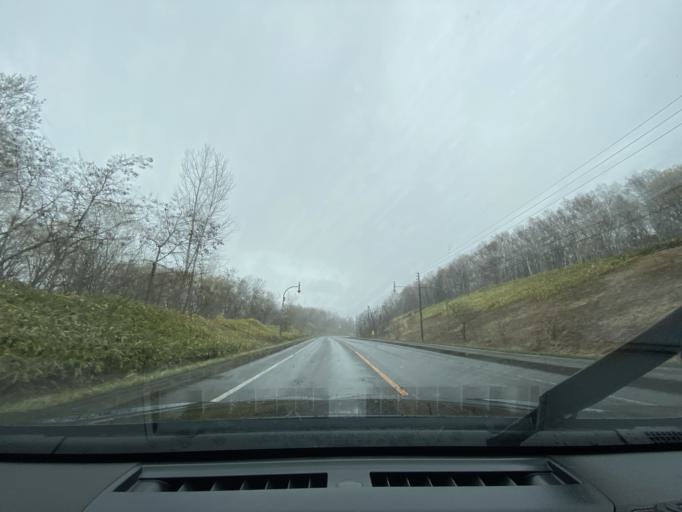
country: JP
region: Hokkaido
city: Fukagawa
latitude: 43.7144
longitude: 142.1736
